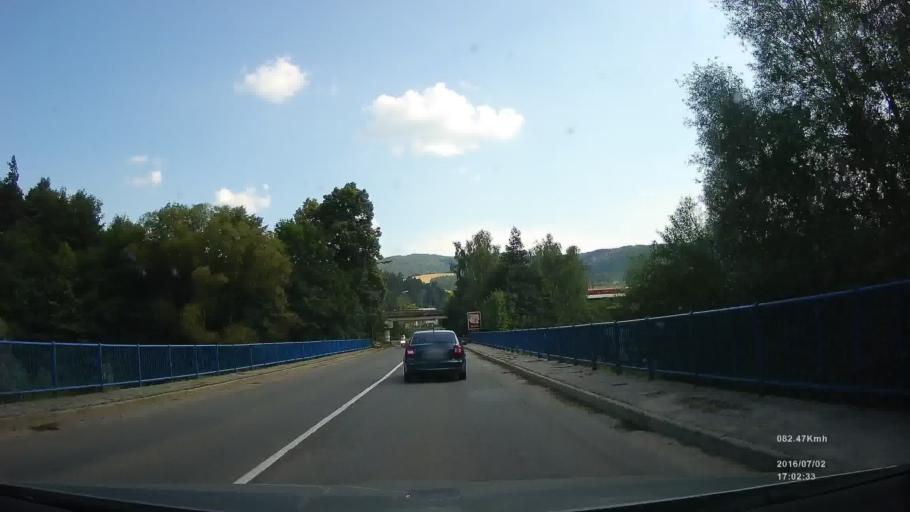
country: SK
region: Kosicky
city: Gelnica
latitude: 48.8791
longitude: 20.9973
